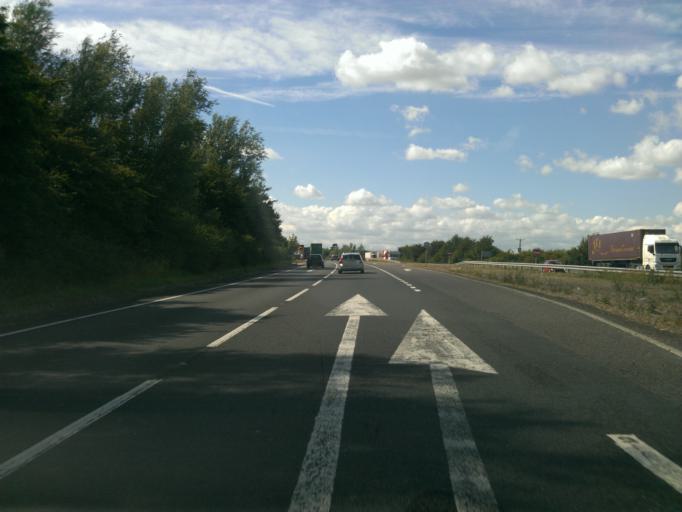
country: GB
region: England
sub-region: Northamptonshire
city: Thrapston
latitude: 52.3865
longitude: -0.4972
